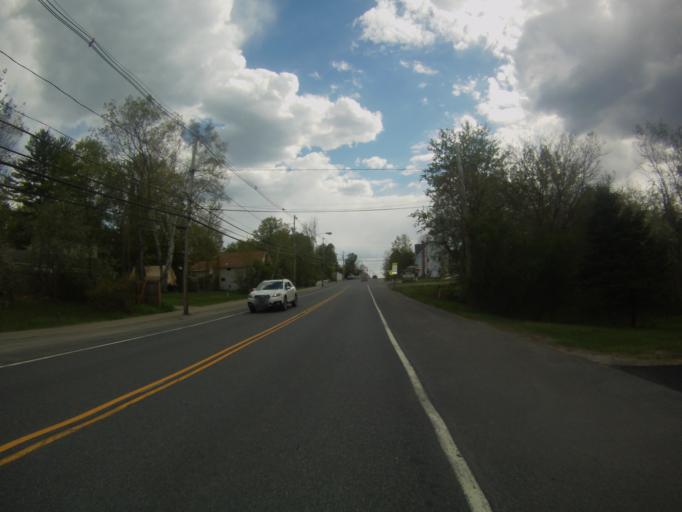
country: US
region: New York
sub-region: Essex County
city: Ticonderoga
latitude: 43.8406
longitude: -73.7603
